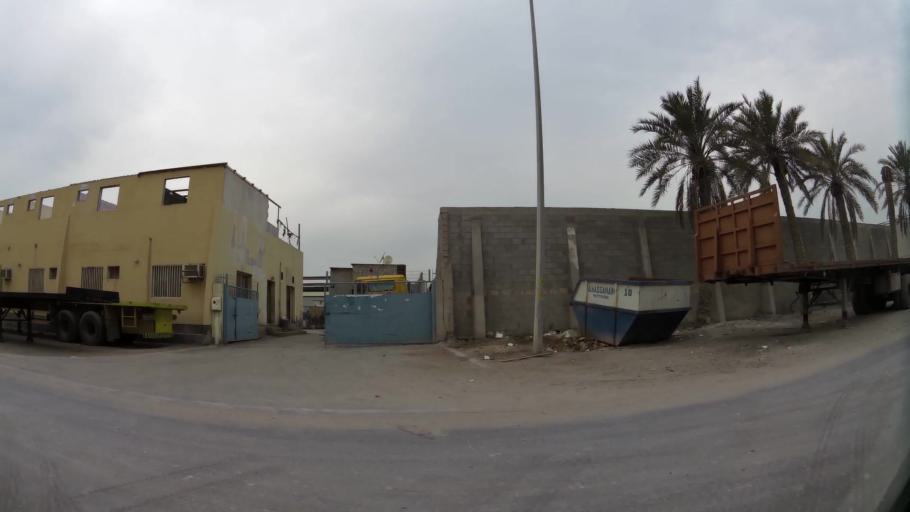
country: BH
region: Northern
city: Sitrah
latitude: 26.1299
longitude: 50.6093
